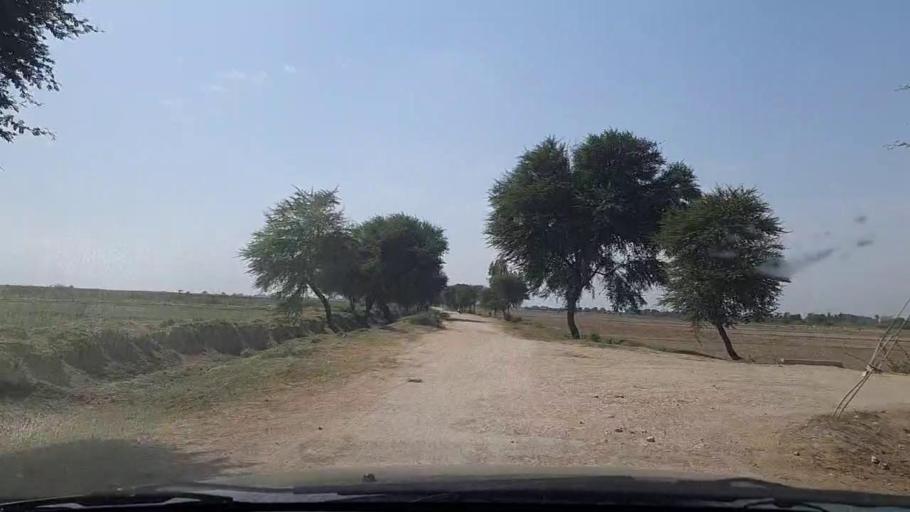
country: PK
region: Sindh
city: Mirpur Batoro
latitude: 24.6109
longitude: 68.2364
